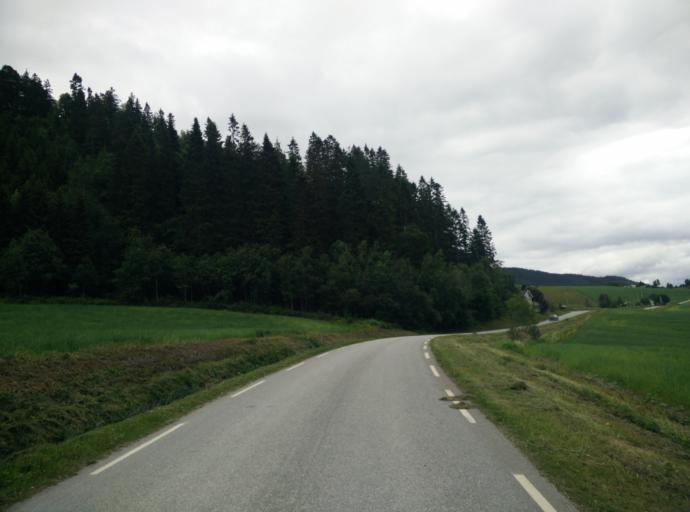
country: NO
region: Sor-Trondelag
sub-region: Skaun
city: Borsa
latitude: 63.3210
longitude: 10.0773
